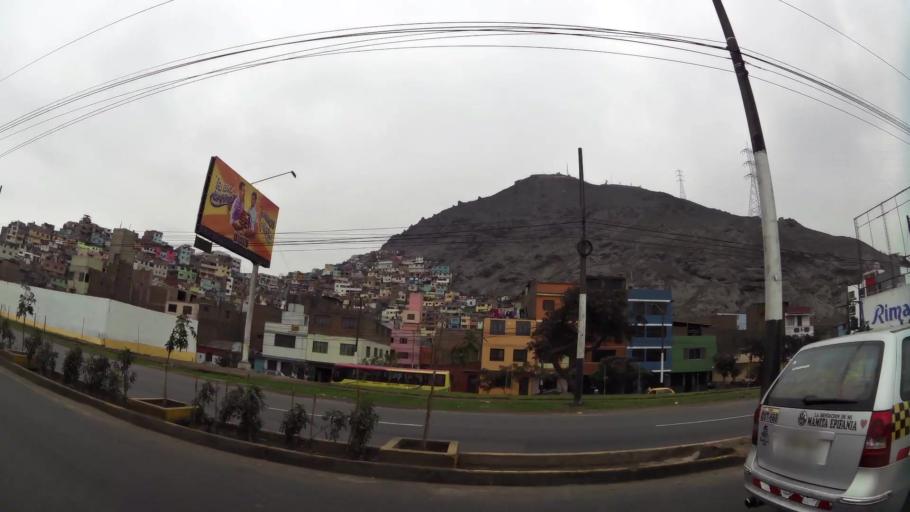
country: PE
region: Lima
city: Lima
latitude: -12.0392
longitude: -77.0161
